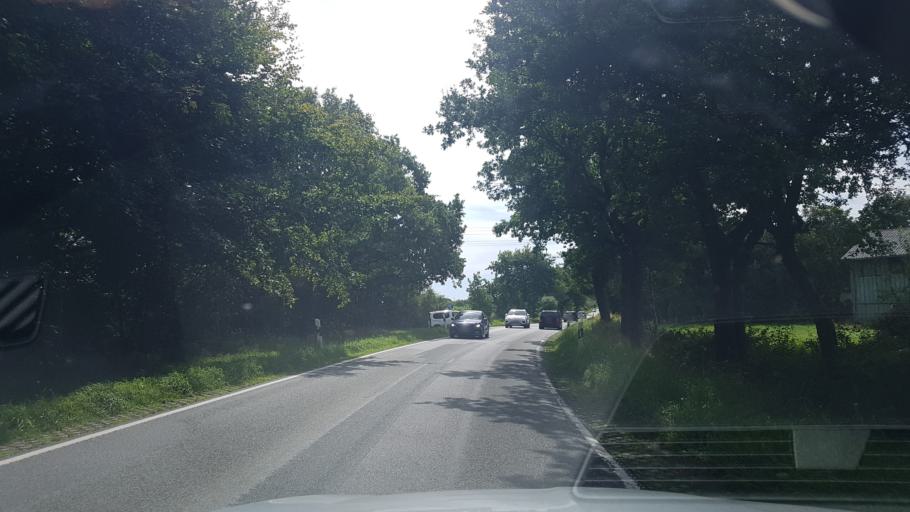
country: DE
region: Schleswig-Holstein
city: Handewitt
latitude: 54.7880
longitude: 9.3196
